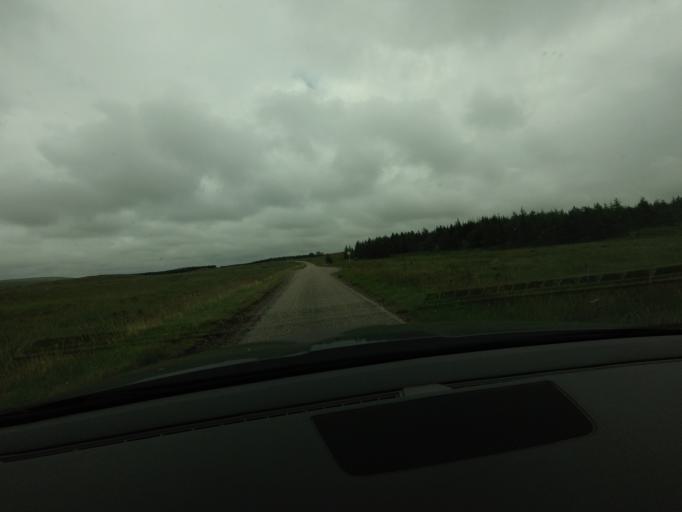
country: GB
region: Scotland
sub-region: Highland
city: Alness
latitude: 58.0973
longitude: -4.4222
